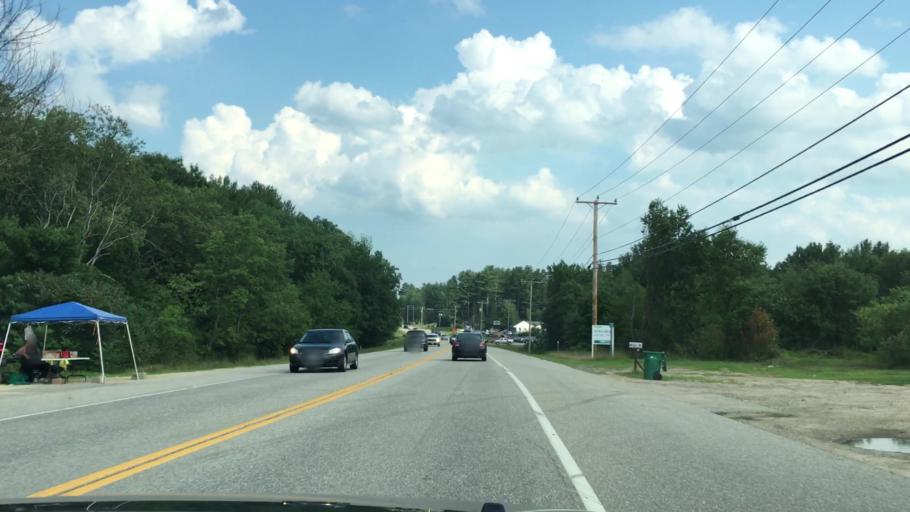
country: US
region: New Hampshire
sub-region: Strafford County
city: Rochester
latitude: 43.3425
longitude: -71.0197
